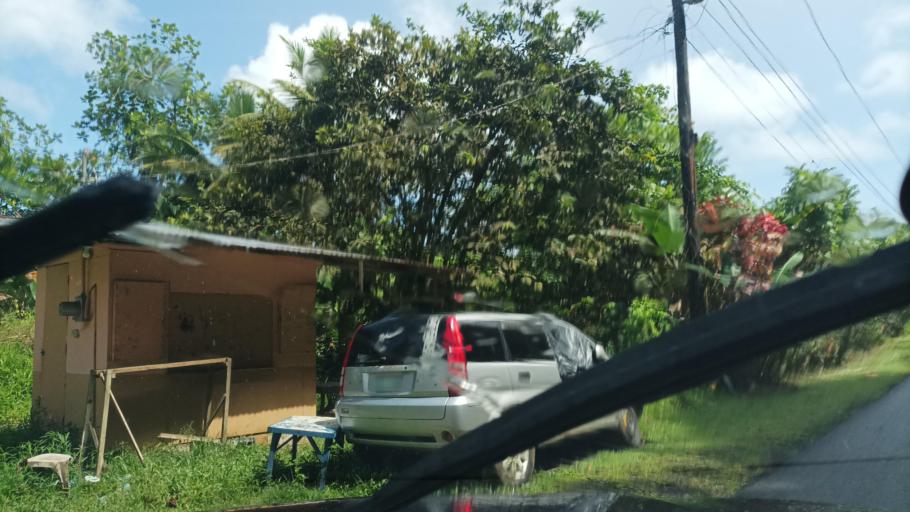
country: FM
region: Pohnpei
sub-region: Kolonia Municipality
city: Kolonia Town
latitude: 6.9452
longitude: 158.1851
